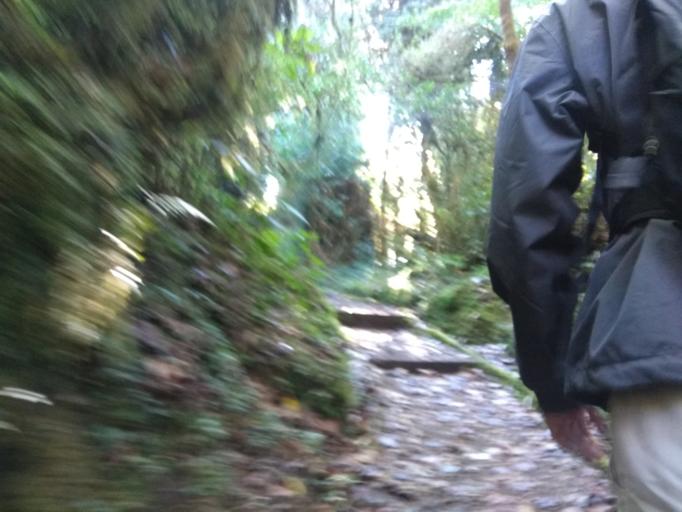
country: CR
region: Heredia
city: Santo Domingo
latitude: 10.1311
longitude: -84.1222
